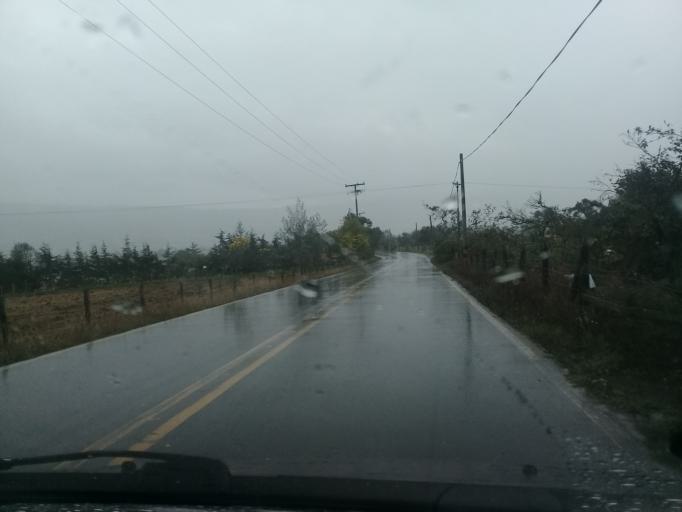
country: CO
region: Cundinamarca
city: Guasca
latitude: 4.8594
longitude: -73.8622
